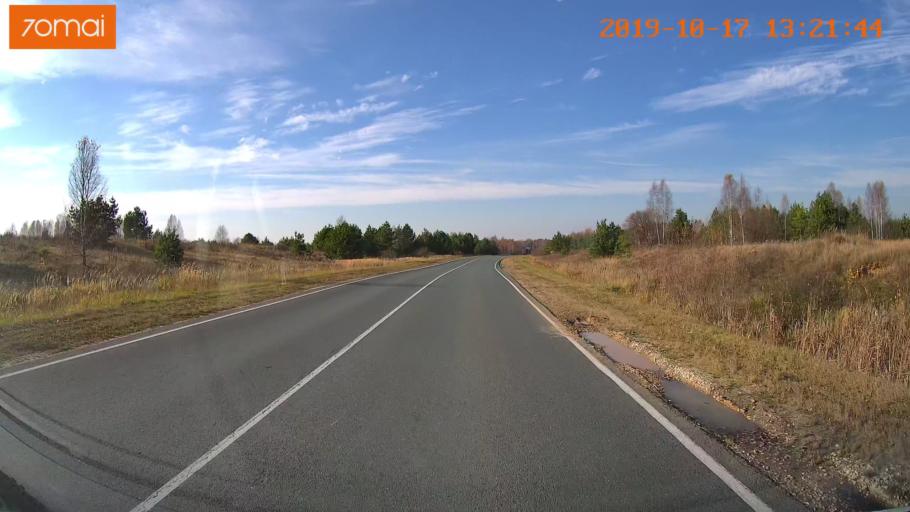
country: RU
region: Rjazan
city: Gus'-Zheleznyy
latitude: 55.0820
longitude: 41.0206
